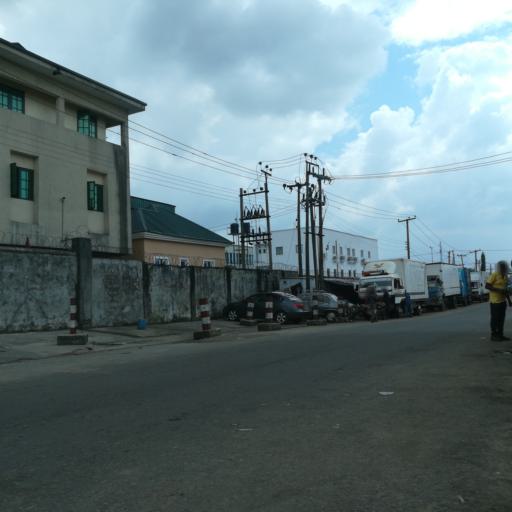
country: NG
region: Rivers
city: Port Harcourt
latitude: 4.8096
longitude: 7.0391
